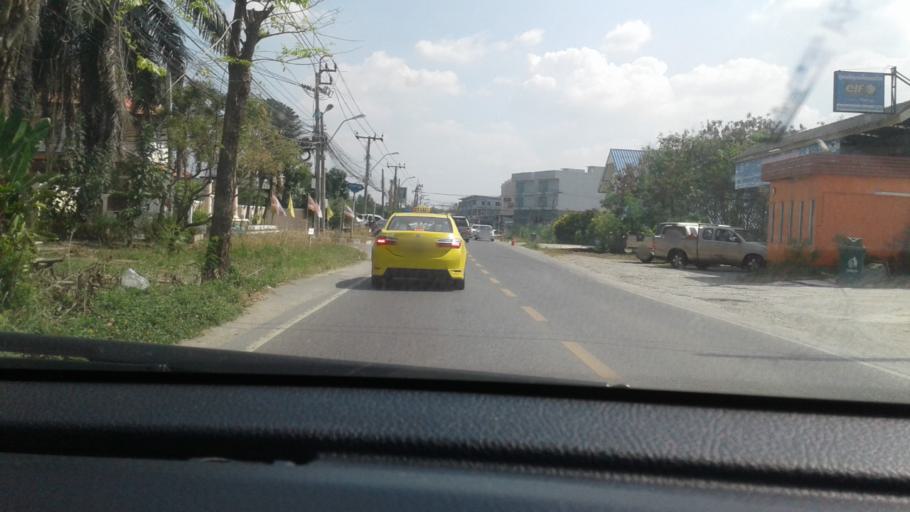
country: TH
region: Bangkok
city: Thawi Watthana
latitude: 13.7973
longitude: 100.3772
